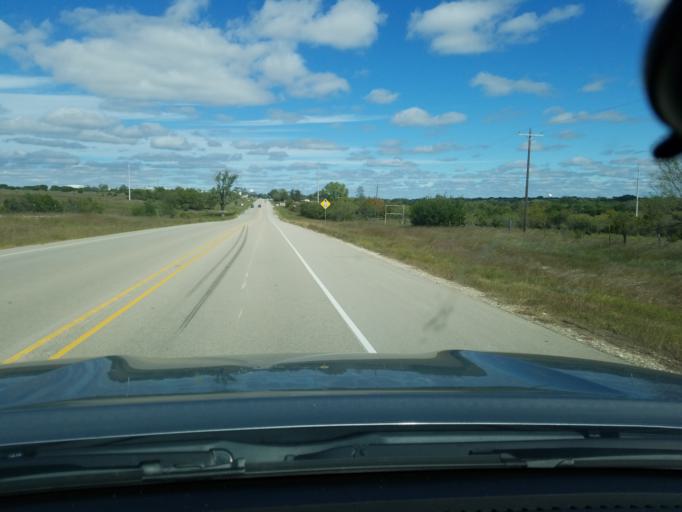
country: US
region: Texas
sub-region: Hamilton County
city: Hamilton
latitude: 31.6839
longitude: -98.1320
